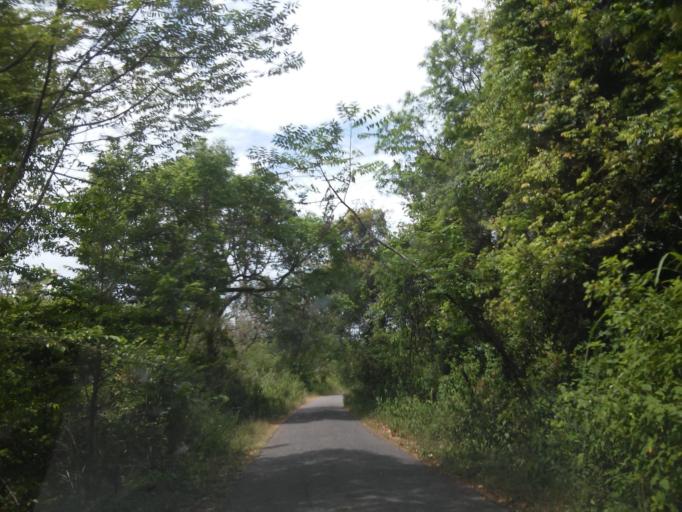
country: LK
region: Central
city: Sigiriya
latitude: 8.0978
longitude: 80.6816
